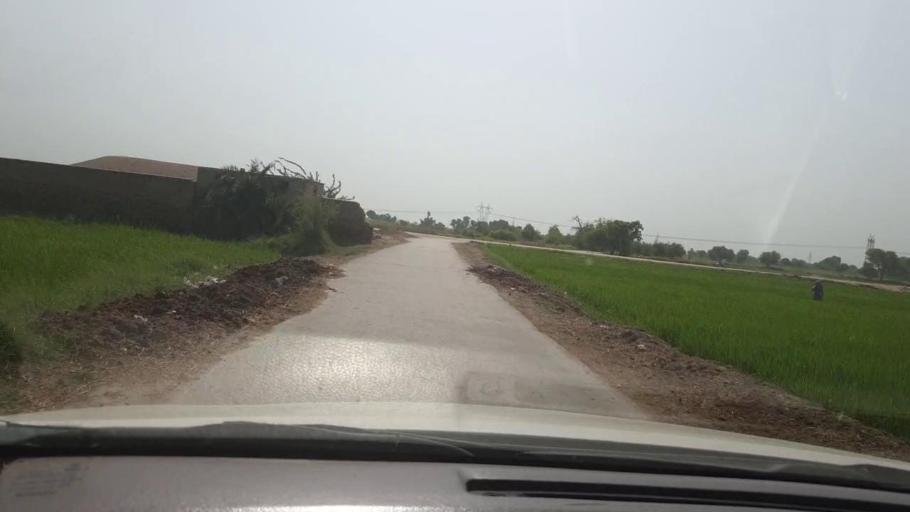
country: PK
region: Sindh
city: Rustam jo Goth
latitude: 27.9764
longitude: 68.8042
